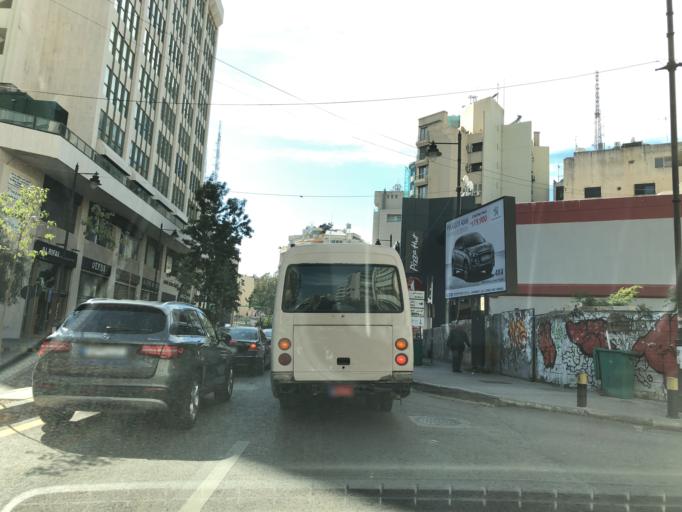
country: LB
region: Beyrouth
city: Beirut
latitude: 33.8877
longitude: 35.5221
